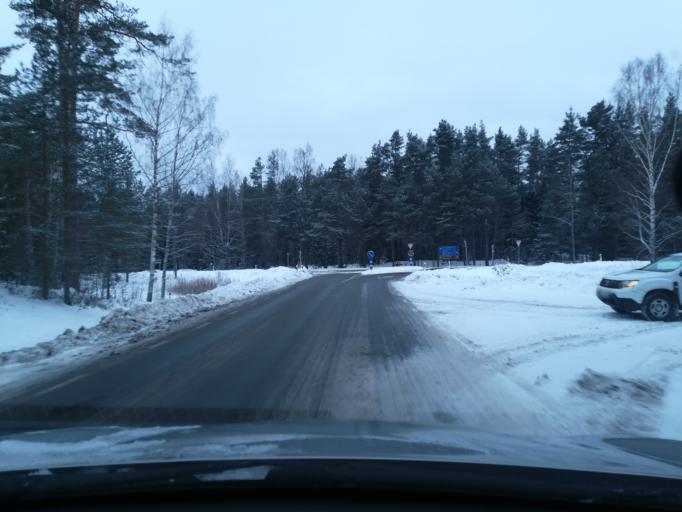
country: EE
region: Harju
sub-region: Keila linn
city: Keila
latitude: 59.3923
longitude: 24.2939
